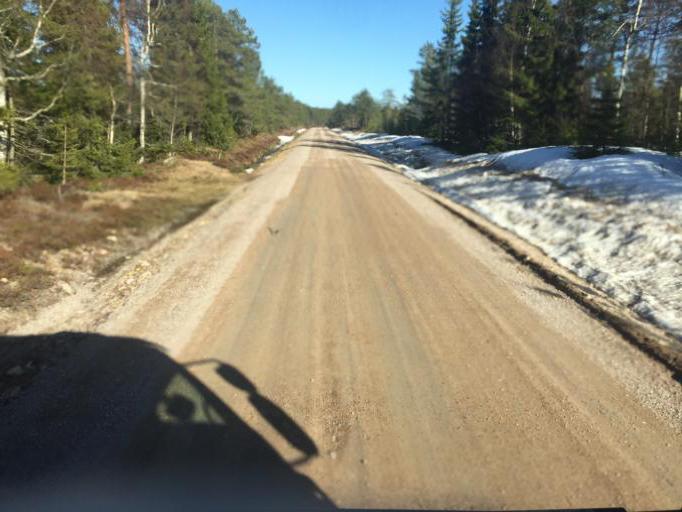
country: SE
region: Vaermland
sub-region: Filipstads Kommun
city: Lesjofors
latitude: 60.2525
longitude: 14.0496
